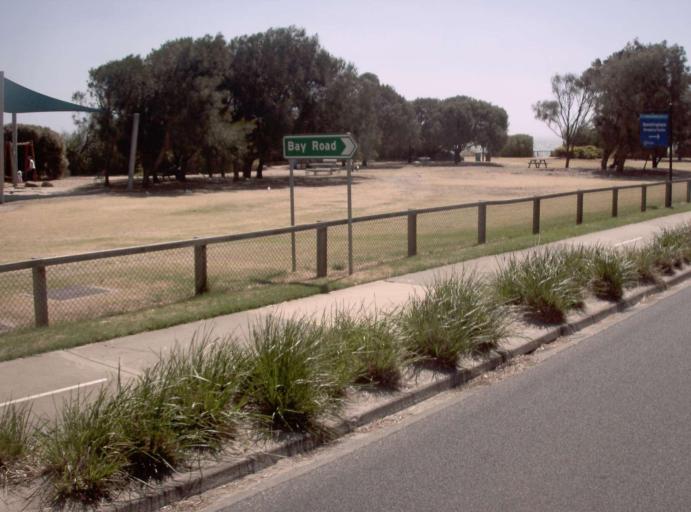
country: AU
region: Victoria
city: Hampton
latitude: -37.9526
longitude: 145.0042
